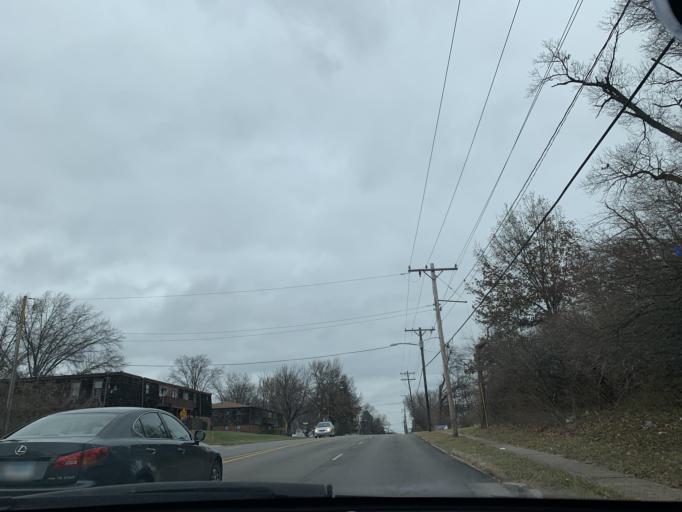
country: US
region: Illinois
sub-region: Sangamon County
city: Leland Grove
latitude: 39.8030
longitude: -89.6870
